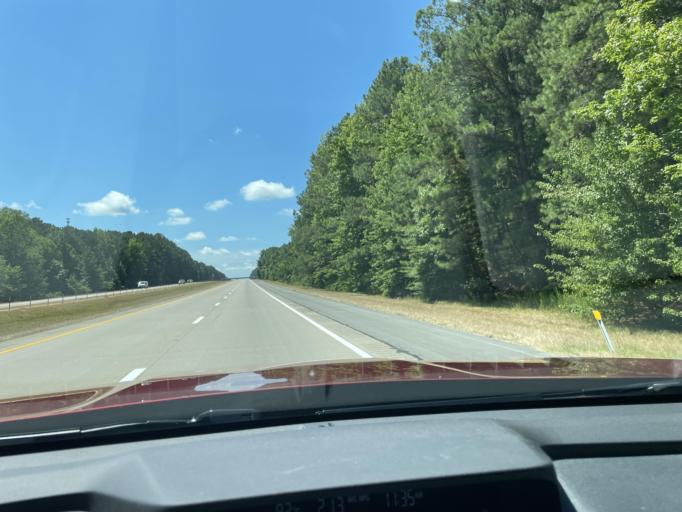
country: US
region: Arkansas
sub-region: Jefferson County
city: Redfield
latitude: 34.4477
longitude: -92.1997
